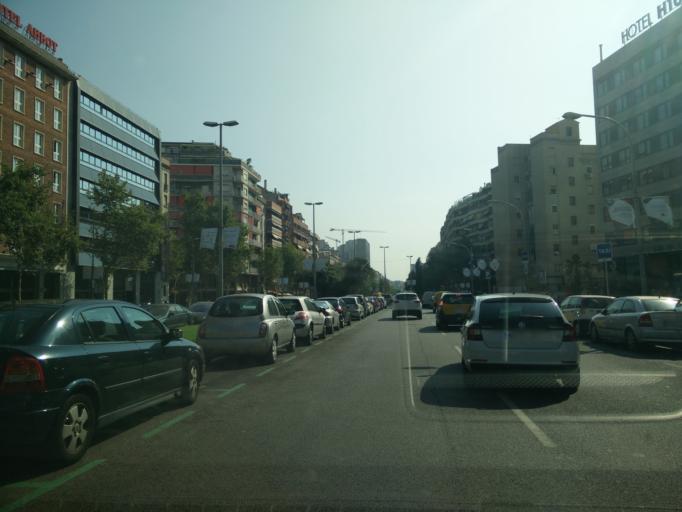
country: ES
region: Catalonia
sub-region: Provincia de Barcelona
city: Sants-Montjuic
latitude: 41.3810
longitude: 2.1447
